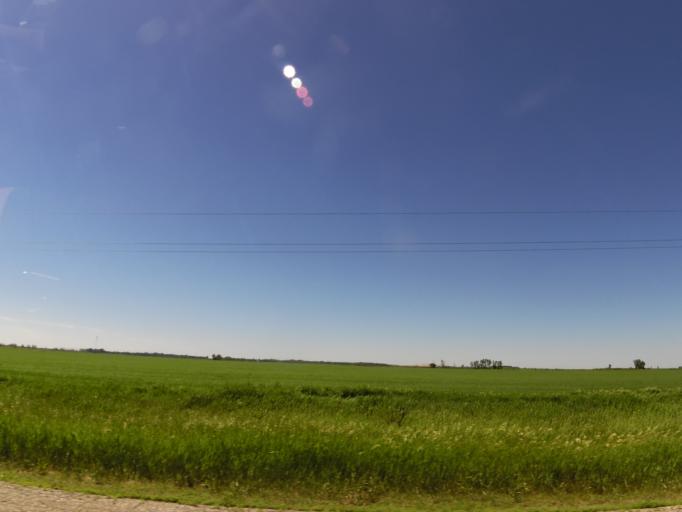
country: US
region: Minnesota
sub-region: Red Lake County
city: Red Lake Falls
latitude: 47.7596
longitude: -96.2782
